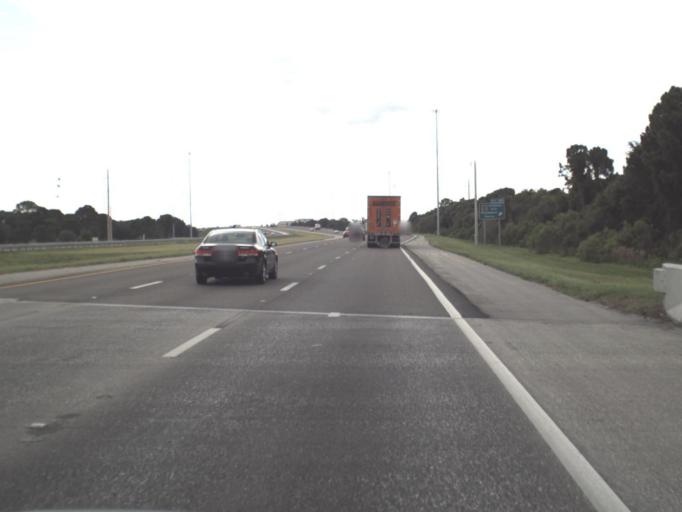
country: US
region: Florida
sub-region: Sarasota County
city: Venice Gardens
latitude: 27.1165
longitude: -82.3915
